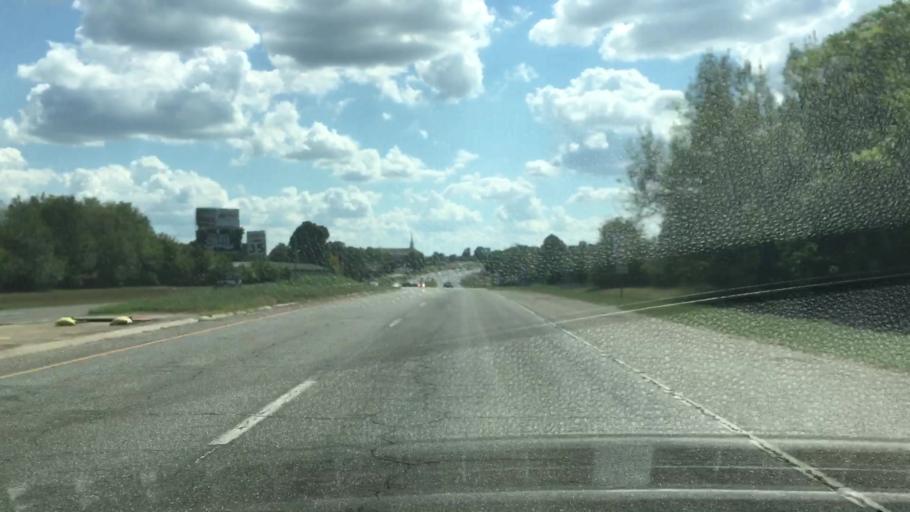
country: US
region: Oklahoma
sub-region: Cherokee County
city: Tahlequah
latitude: 35.9174
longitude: -94.9557
